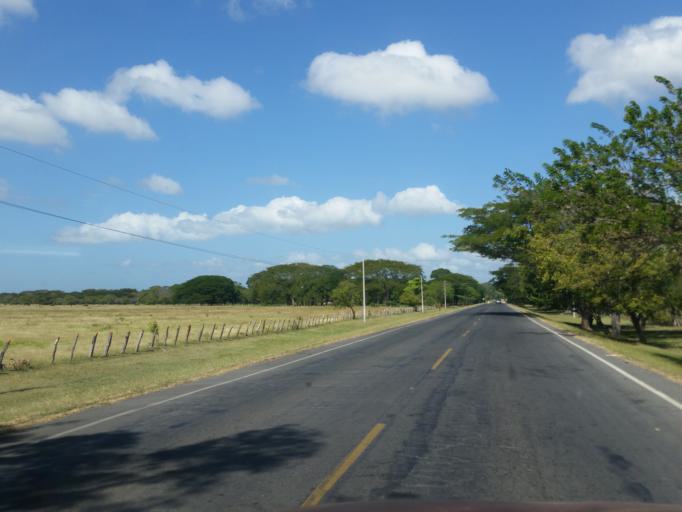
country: NI
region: Granada
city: Nandaime
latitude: 11.7072
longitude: -86.0062
